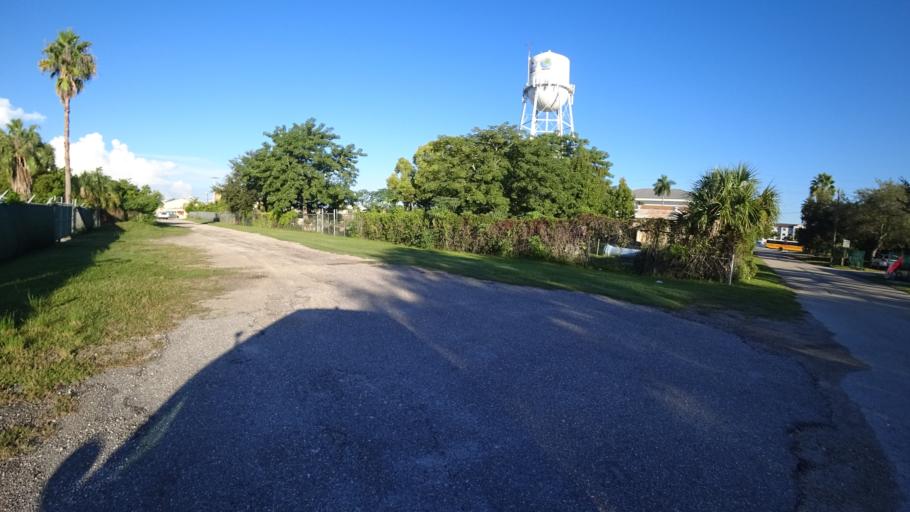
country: US
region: Florida
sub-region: Manatee County
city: Bradenton
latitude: 27.4928
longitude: -82.5642
